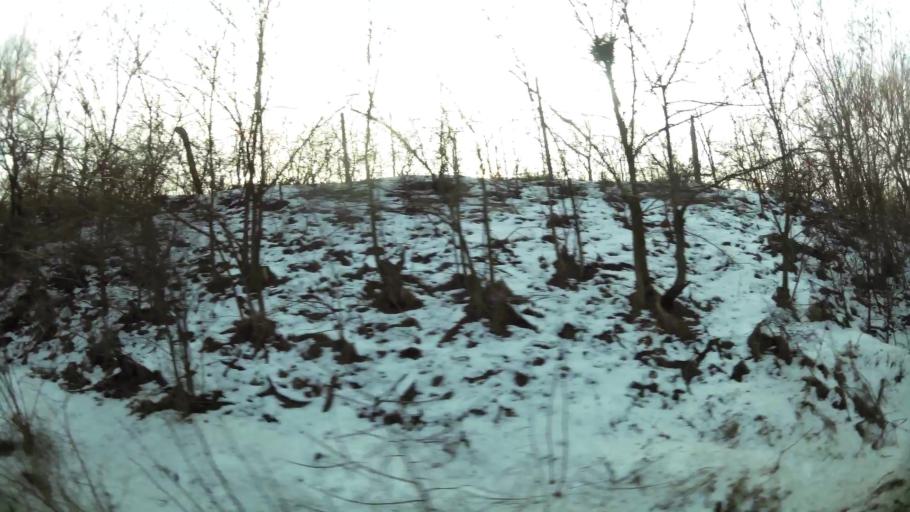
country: MK
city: Miladinovci
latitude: 41.9764
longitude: 21.6304
